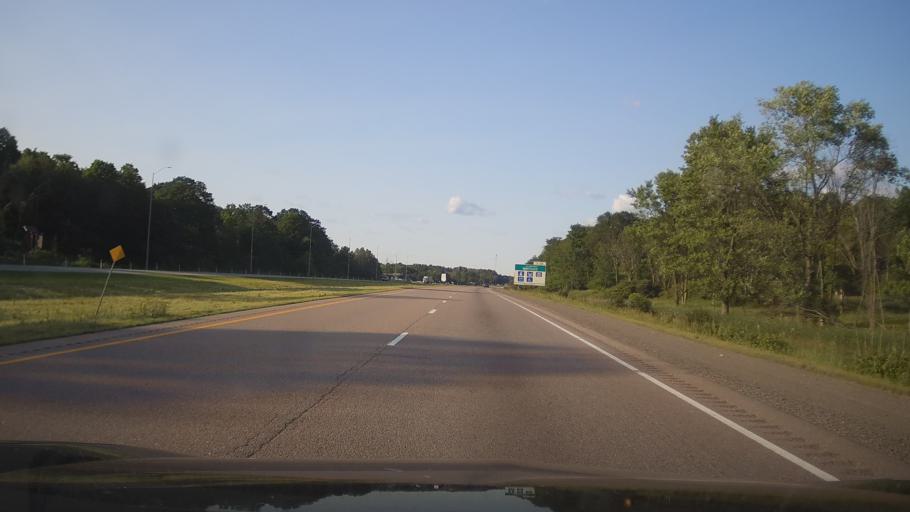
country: US
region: New York
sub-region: Jefferson County
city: Alexandria Bay
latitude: 44.4829
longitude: -75.8615
